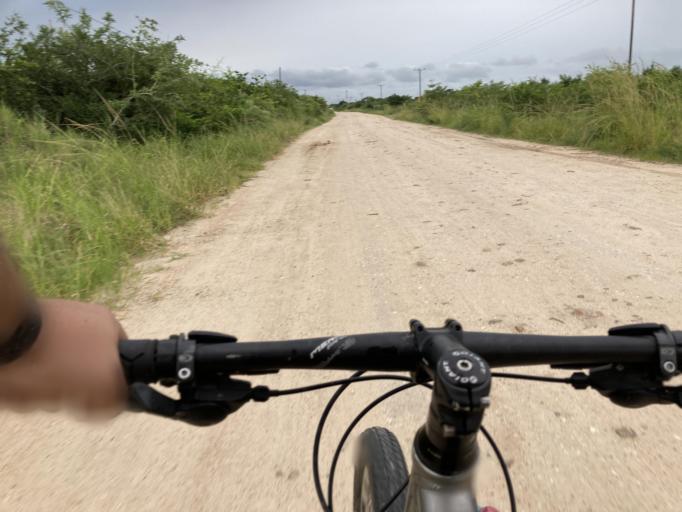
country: MZ
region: Maputo City
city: Maputo
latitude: -26.0526
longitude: 32.5318
